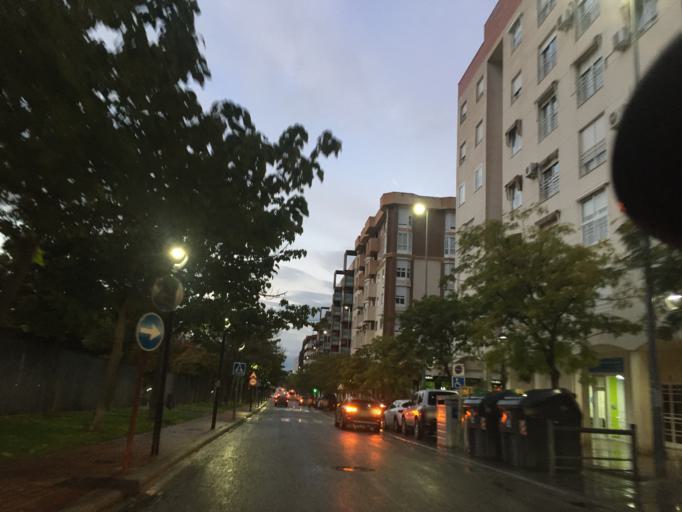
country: ES
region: Andalusia
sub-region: Provincia de Jaen
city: Jaen
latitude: 37.7861
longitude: -3.7899
